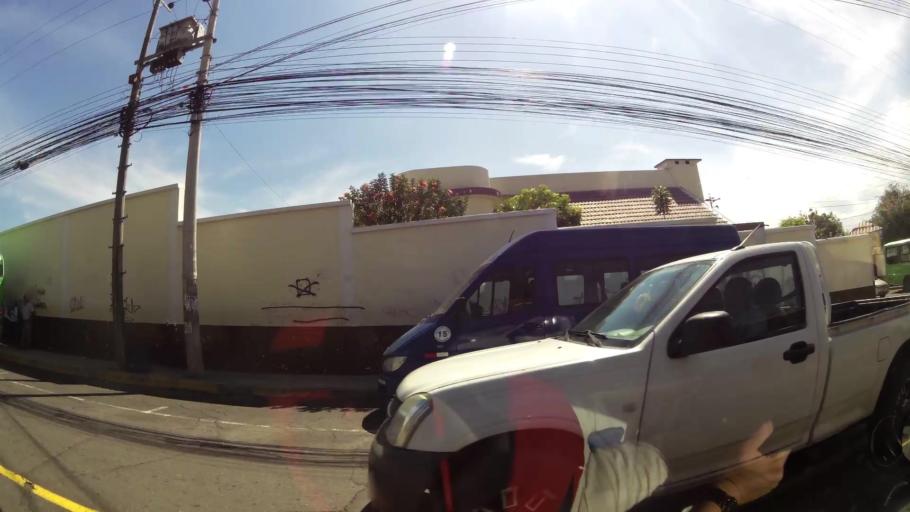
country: EC
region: Pichincha
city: Quito
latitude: -0.2025
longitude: -78.4297
